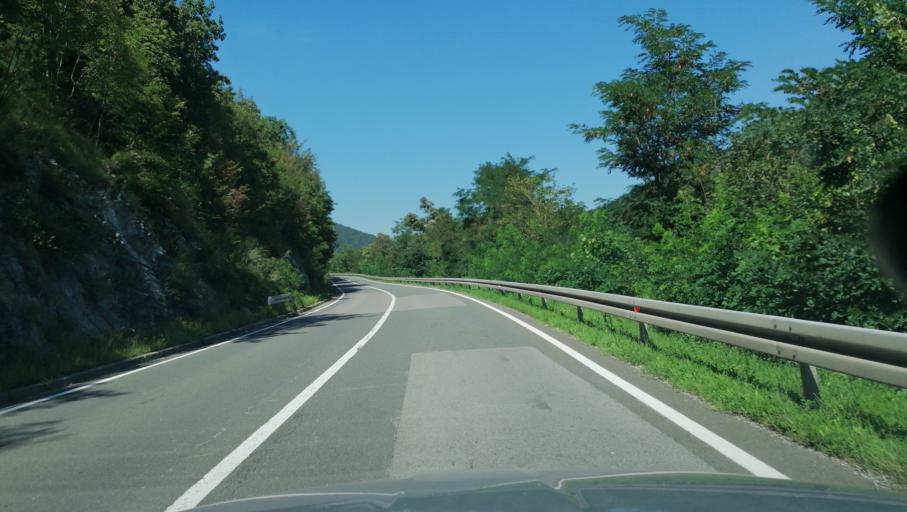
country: RS
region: Central Serbia
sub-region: Raski Okrug
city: Kraljevo
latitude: 43.6391
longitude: 20.5511
